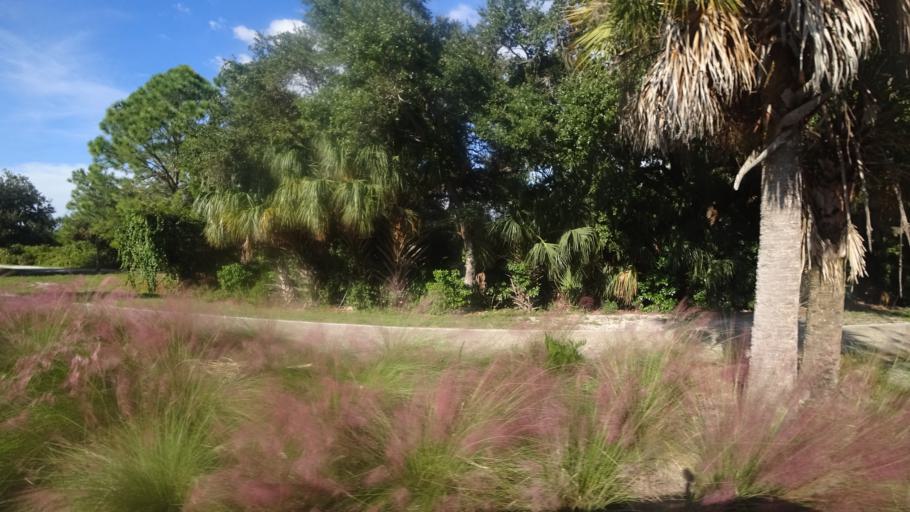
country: US
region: Florida
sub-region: Manatee County
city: West Bradenton
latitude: 27.5334
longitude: -82.6260
